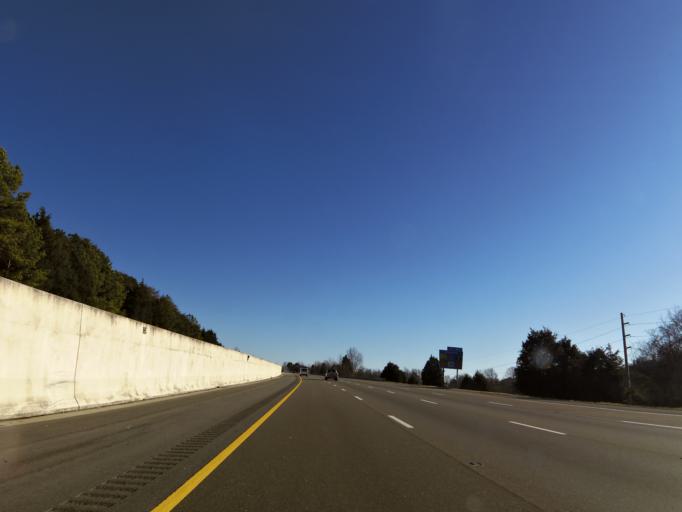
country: US
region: Tennessee
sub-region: Jefferson County
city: Dandridge
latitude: 36.0243
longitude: -83.4704
